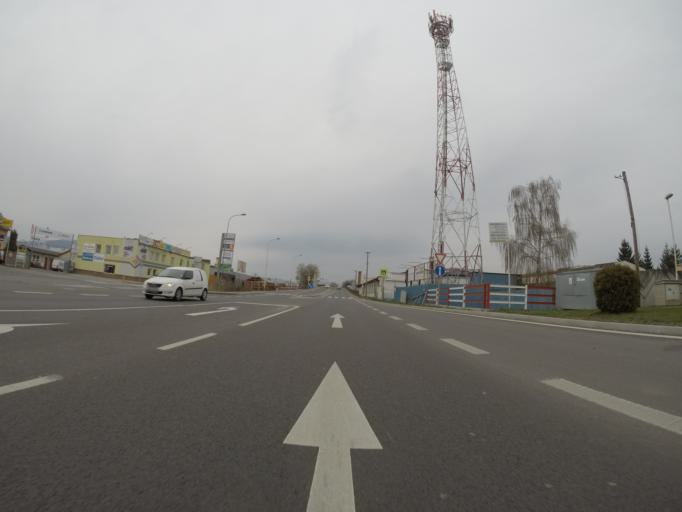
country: SK
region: Nitriansky
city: Prievidza
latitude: 48.7640
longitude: 18.6245
